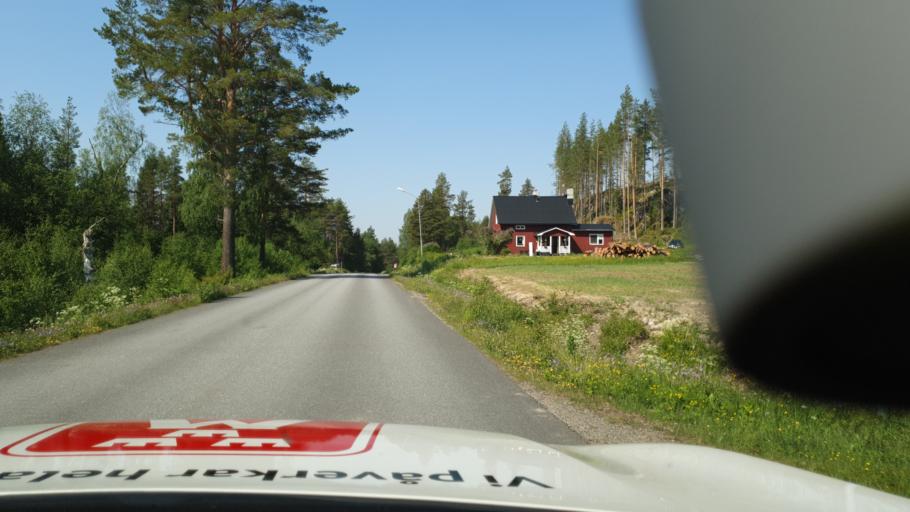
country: SE
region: Vaesterbotten
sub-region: Skelleftea Kommun
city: Langsele
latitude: 64.9413
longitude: 19.9734
